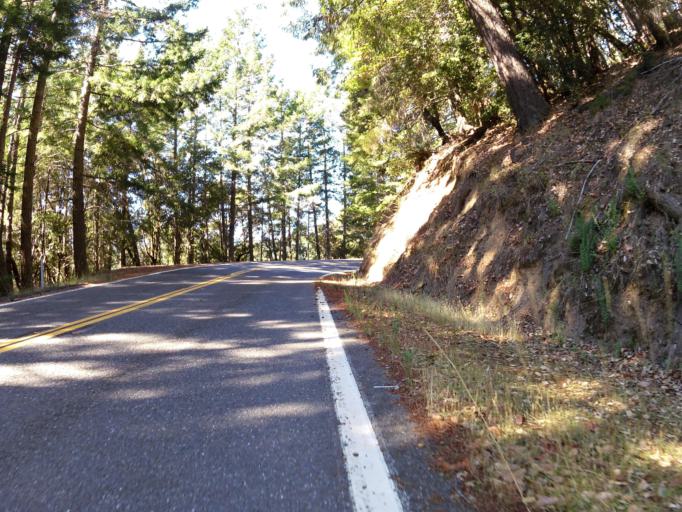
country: US
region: California
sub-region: Humboldt County
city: Redway
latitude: 39.8493
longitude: -123.7411
